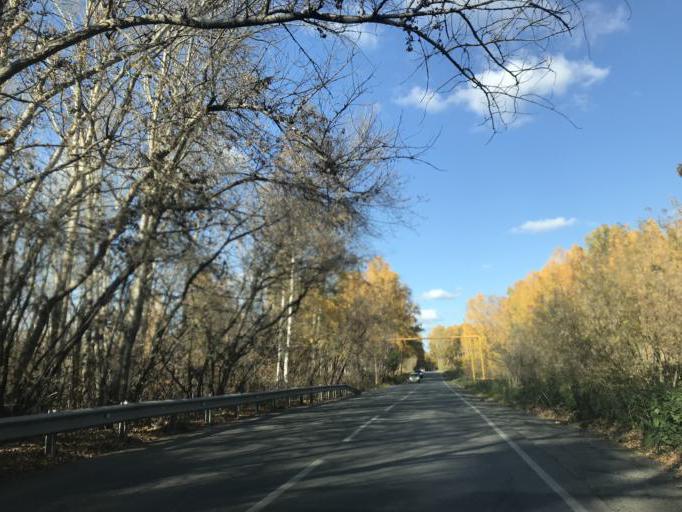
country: RU
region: Chelyabinsk
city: Dolgoderevenskoye
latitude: 55.2631
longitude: 61.3644
